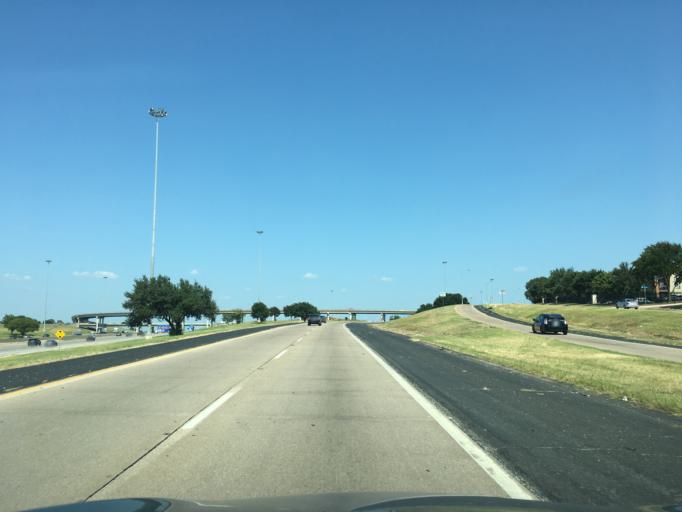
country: US
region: Texas
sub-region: Tarrant County
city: Kennedale
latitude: 32.6688
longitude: -97.2135
